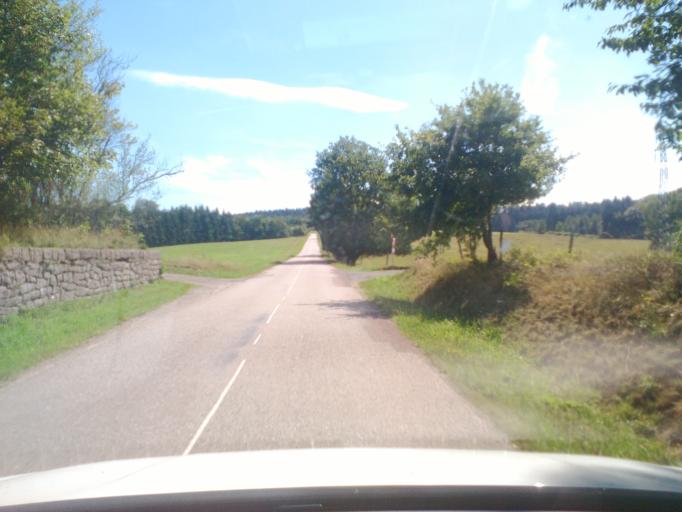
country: FR
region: Lorraine
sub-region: Departement des Vosges
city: Senones
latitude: 48.3764
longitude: 6.9701
